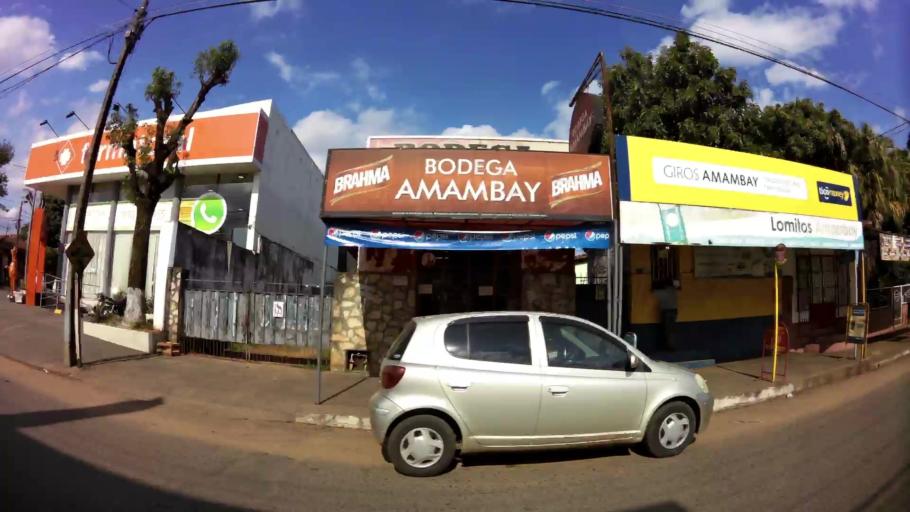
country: PY
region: Central
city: Fernando de la Mora
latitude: -25.3291
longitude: -57.5303
